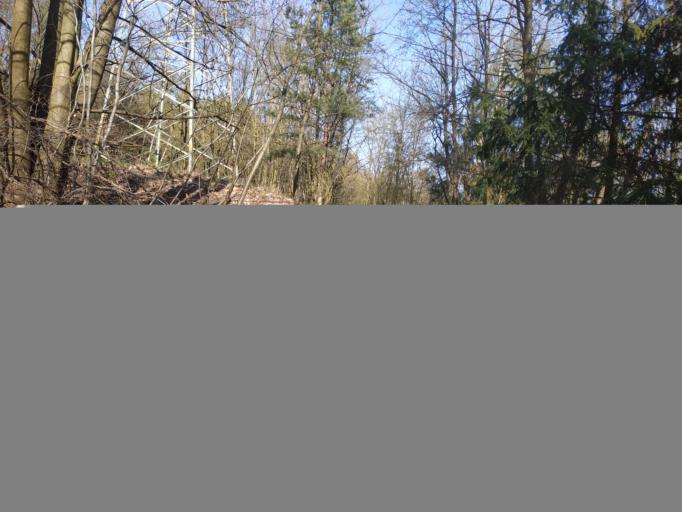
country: DE
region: Brandenburg
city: Strausberg
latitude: 52.5669
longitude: 13.8318
